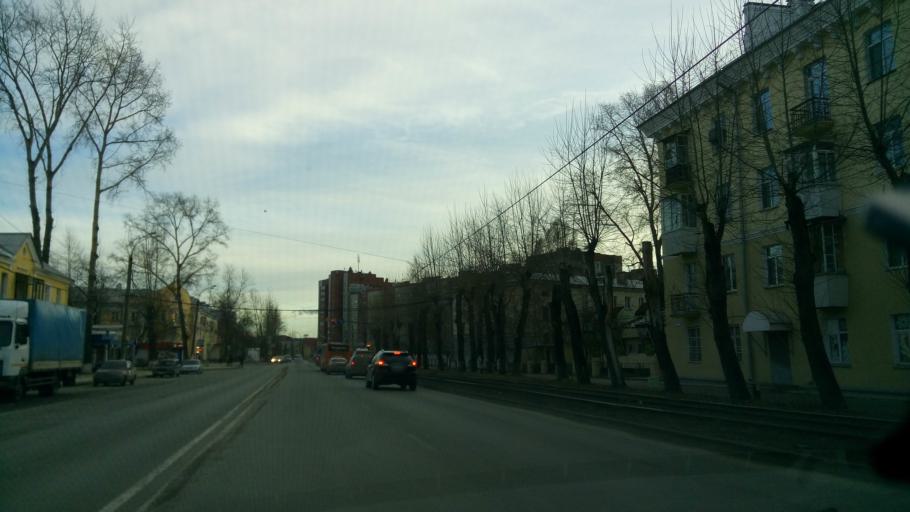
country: RU
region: Sverdlovsk
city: Shuvakish
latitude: 56.8729
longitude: 60.5193
